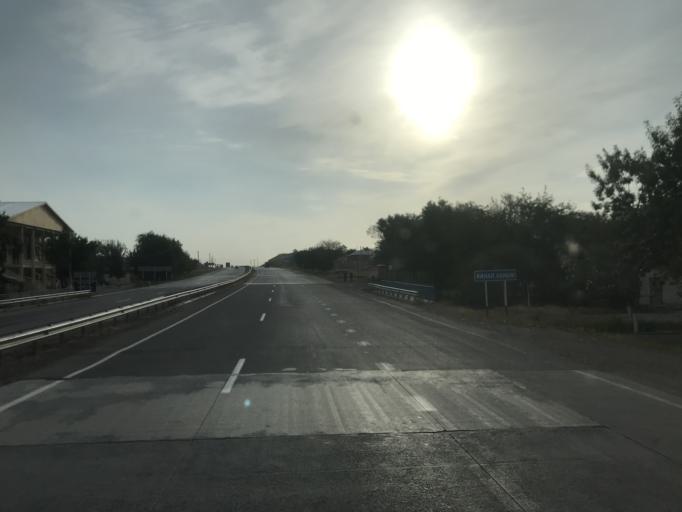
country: UZ
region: Toshkent
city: Salor
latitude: 41.5047
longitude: 69.3705
